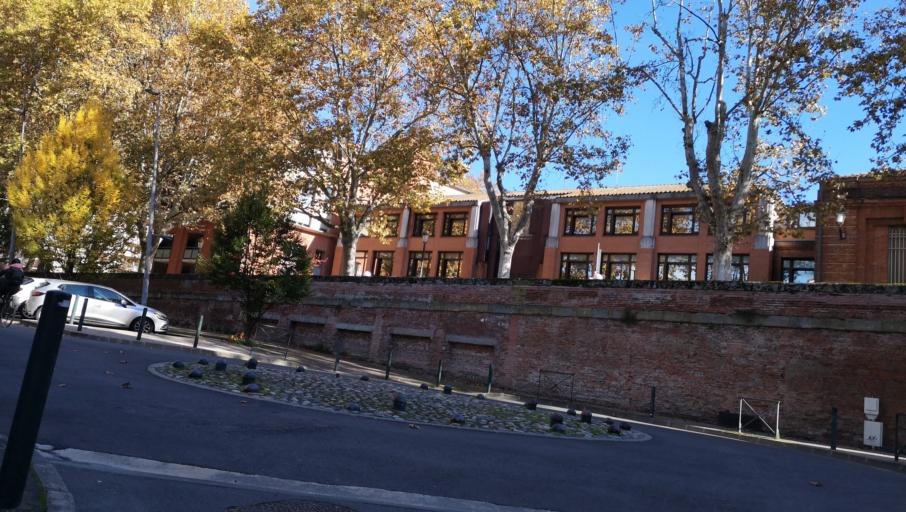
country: FR
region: Midi-Pyrenees
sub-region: Departement de la Haute-Garonne
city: Toulouse
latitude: 43.6048
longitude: 1.4322
